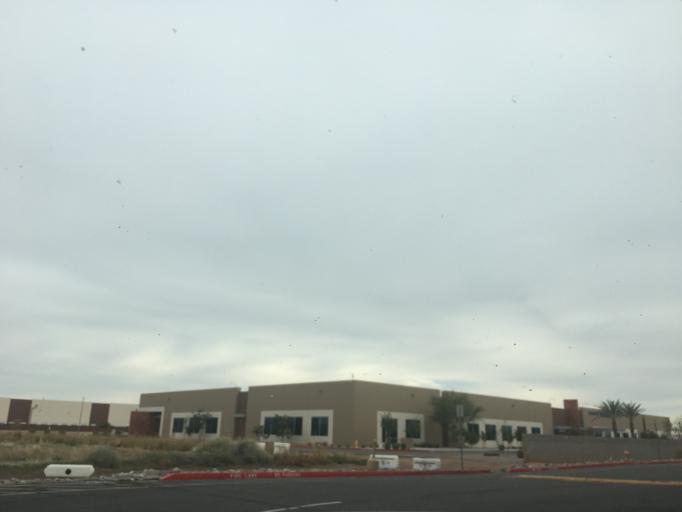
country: US
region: Arizona
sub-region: Maricopa County
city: San Carlos
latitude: 33.3483
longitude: -111.8287
